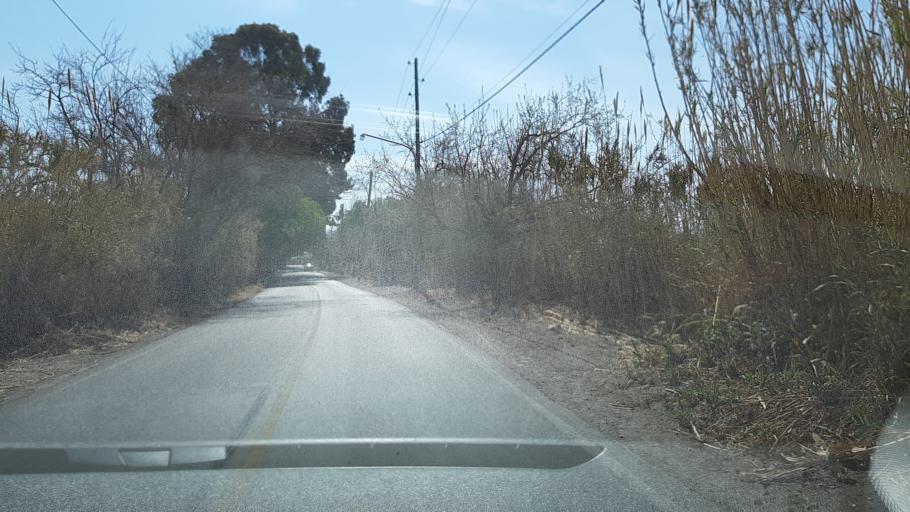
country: AR
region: San Juan
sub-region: Departamento de Rivadavia
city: Rivadavia
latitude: -31.5258
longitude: -68.6194
